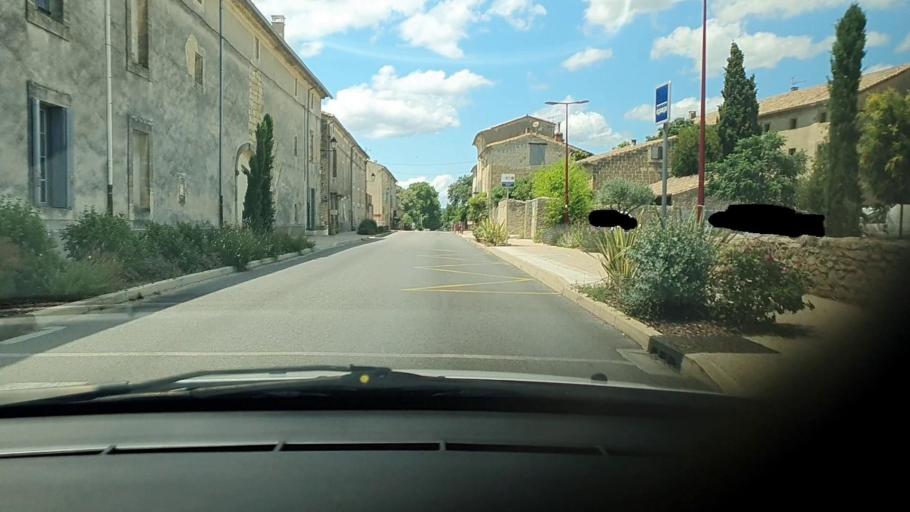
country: FR
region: Languedoc-Roussillon
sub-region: Departement du Gard
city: Montaren-et-Saint-Mediers
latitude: 44.0279
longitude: 4.3806
